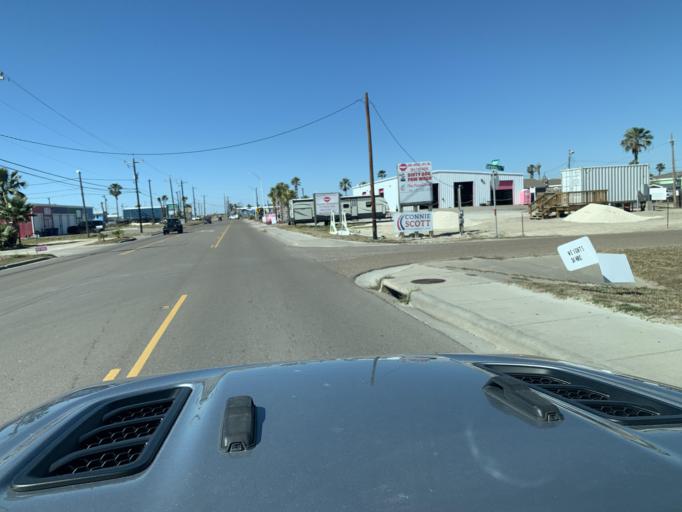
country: US
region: Texas
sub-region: Nueces County
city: Port Aransas
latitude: 27.8298
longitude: -97.0692
